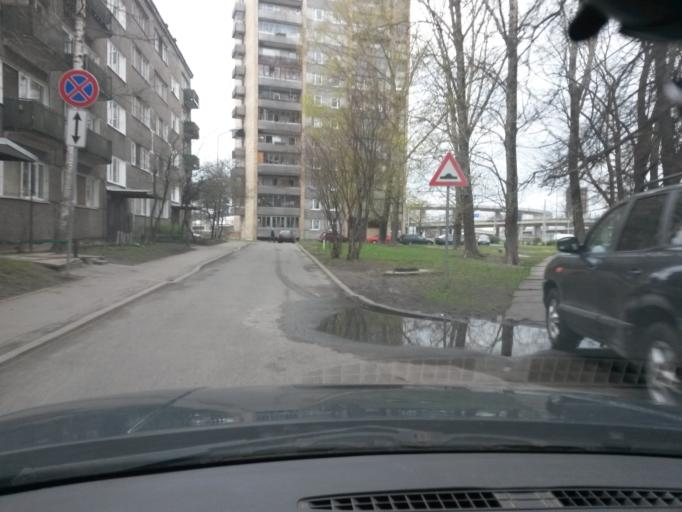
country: LV
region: Riga
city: Riga
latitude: 56.9223
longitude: 24.1728
